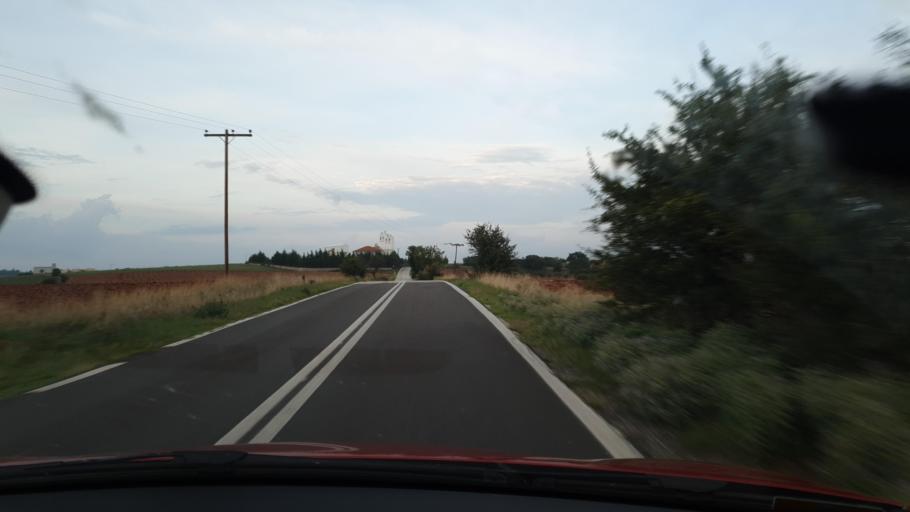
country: GR
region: Central Macedonia
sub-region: Nomos Kilkis
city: Kristoni
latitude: 40.9544
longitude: 22.8375
